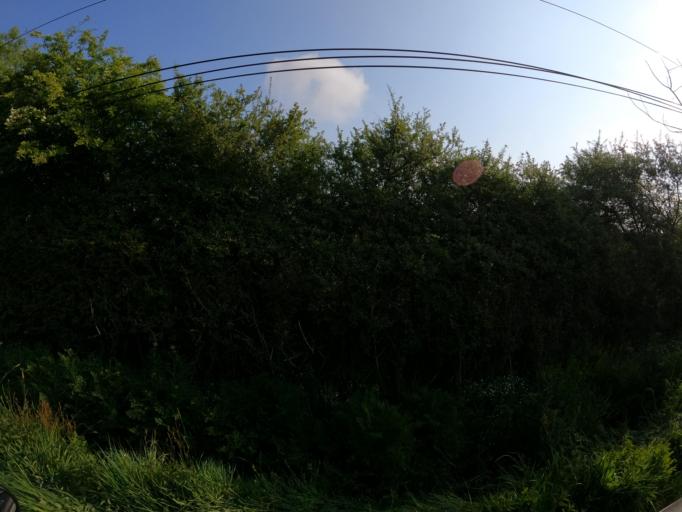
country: FR
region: Pays de la Loire
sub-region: Departement de Maine-et-Loire
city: La Romagne
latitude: 47.0718
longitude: -1.0032
